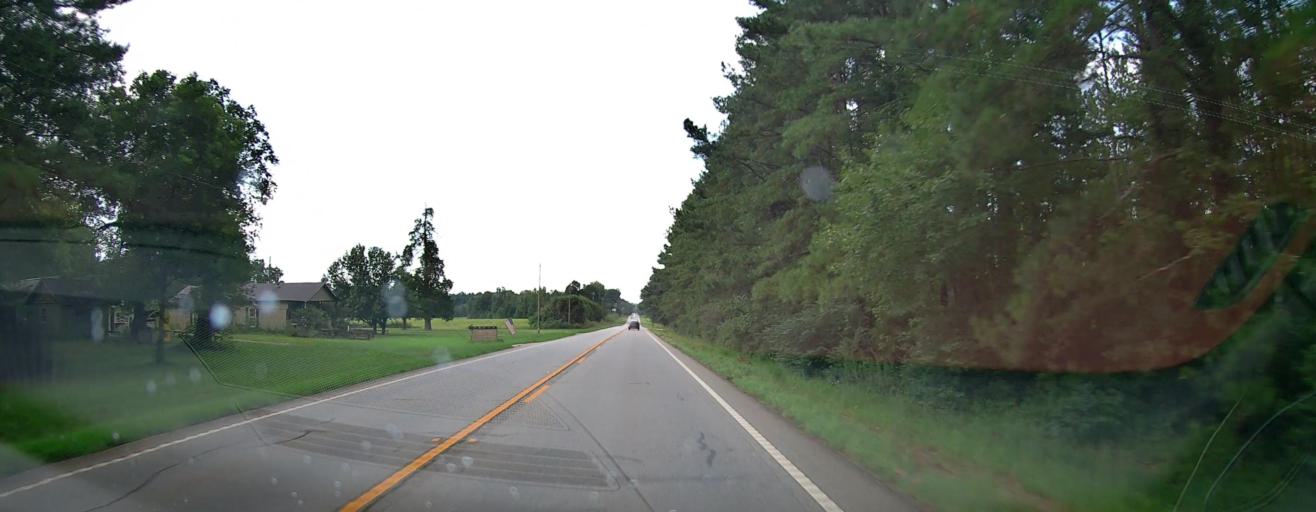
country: US
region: Georgia
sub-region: Coweta County
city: Senoia
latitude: 33.1958
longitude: -84.5802
